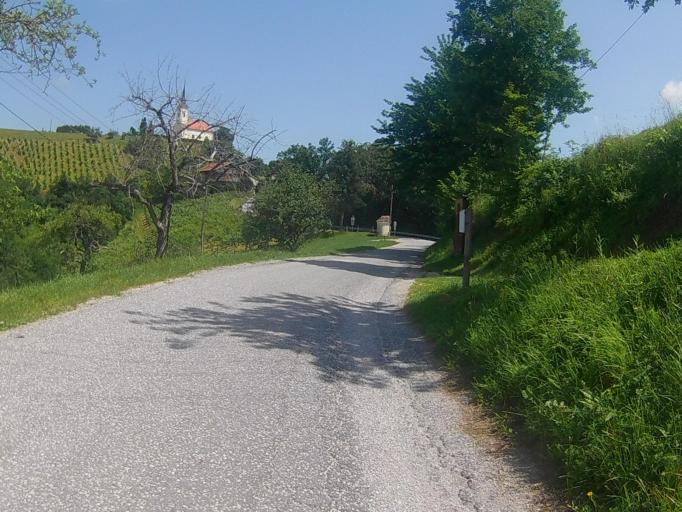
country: SI
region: Maribor
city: Kamnica
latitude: 46.6012
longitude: 15.6044
